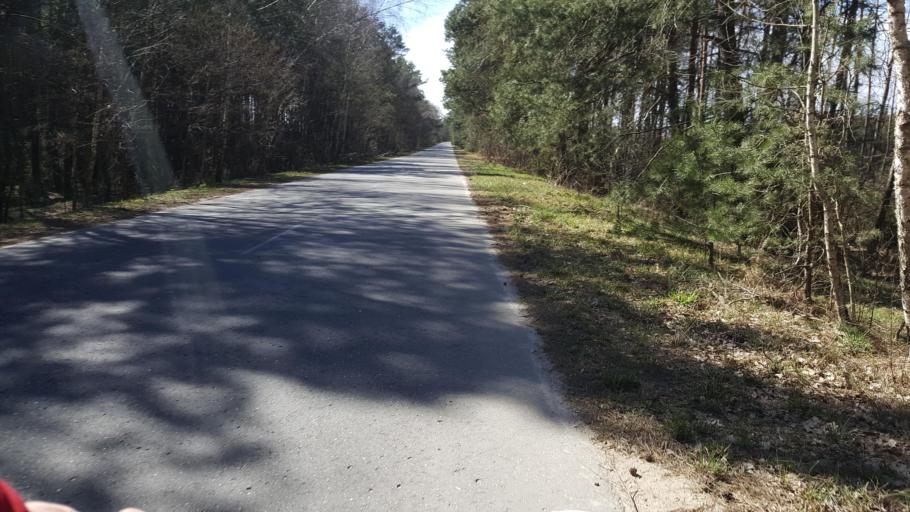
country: BY
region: Brest
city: Charnawchytsy
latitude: 52.2898
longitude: 23.7899
